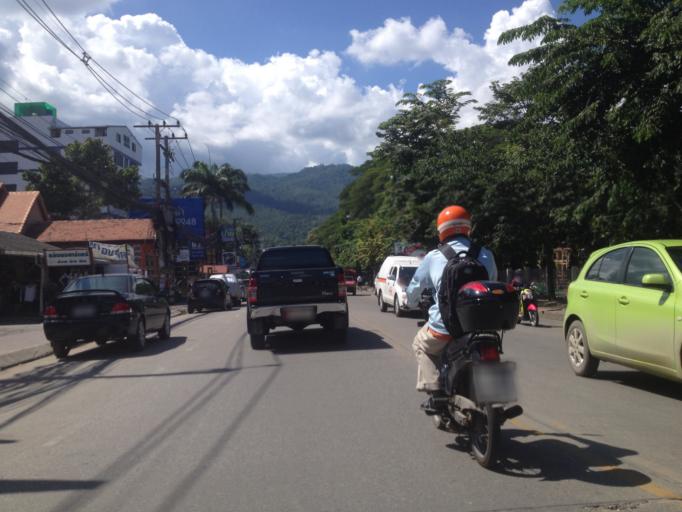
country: TH
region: Chiang Mai
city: Chiang Mai
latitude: 18.7923
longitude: 98.9567
